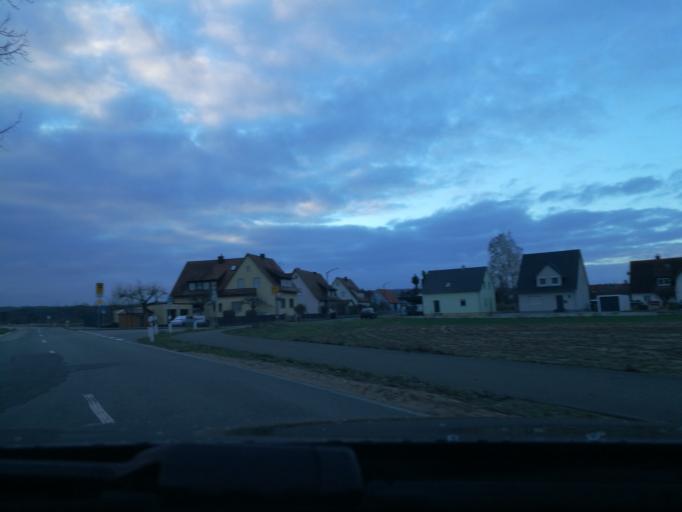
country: DE
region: Bavaria
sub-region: Regierungsbezirk Mittelfranken
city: Baiersdorf
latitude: 49.6494
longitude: 11.0456
